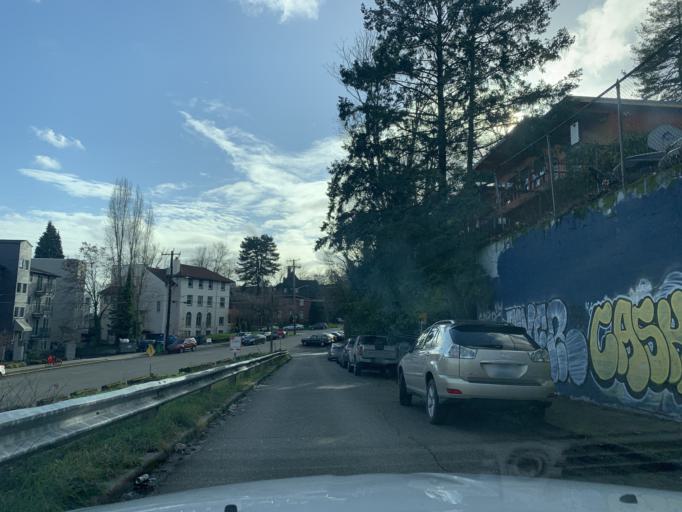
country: US
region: Washington
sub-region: King County
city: Seattle
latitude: 47.6629
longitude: -122.3045
